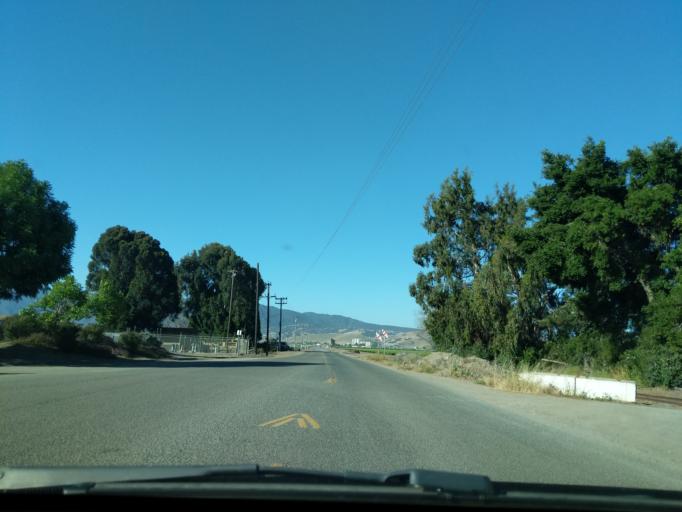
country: US
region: California
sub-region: Monterey County
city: Salinas
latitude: 36.6454
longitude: -121.6337
